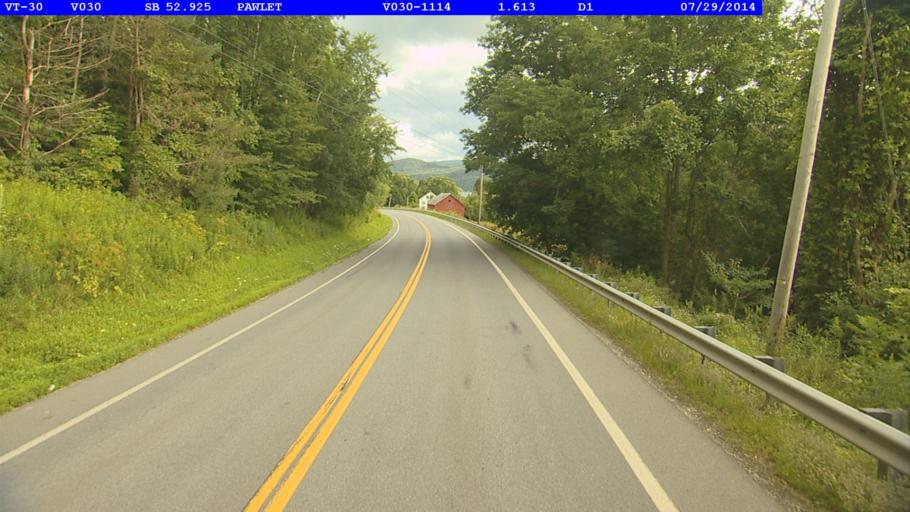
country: US
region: New York
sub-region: Washington County
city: Granville
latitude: 43.3333
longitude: -73.1763
